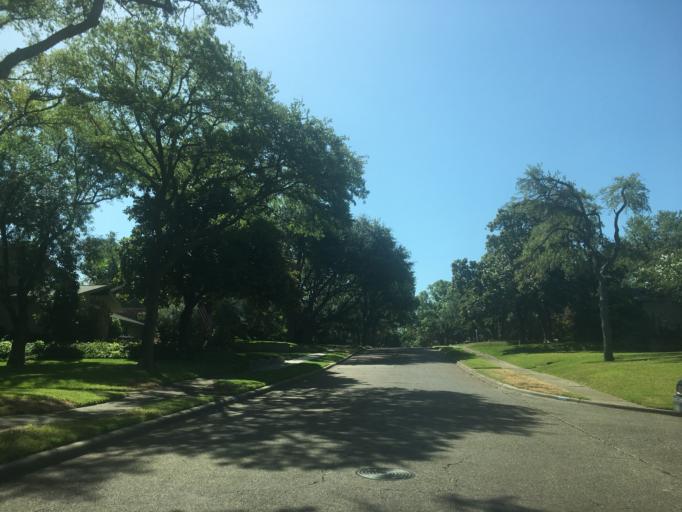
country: US
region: Texas
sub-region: Dallas County
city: Highland Park
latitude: 32.8701
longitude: -96.7259
